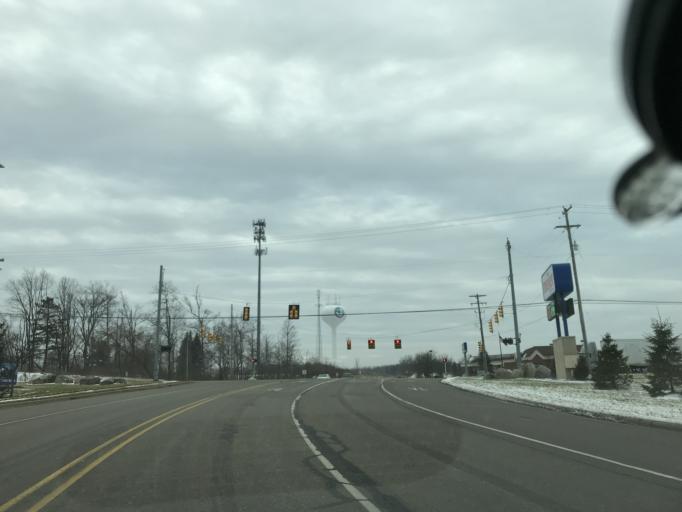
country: US
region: Michigan
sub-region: Kent County
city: Rockford
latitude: 43.1177
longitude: -85.5999
